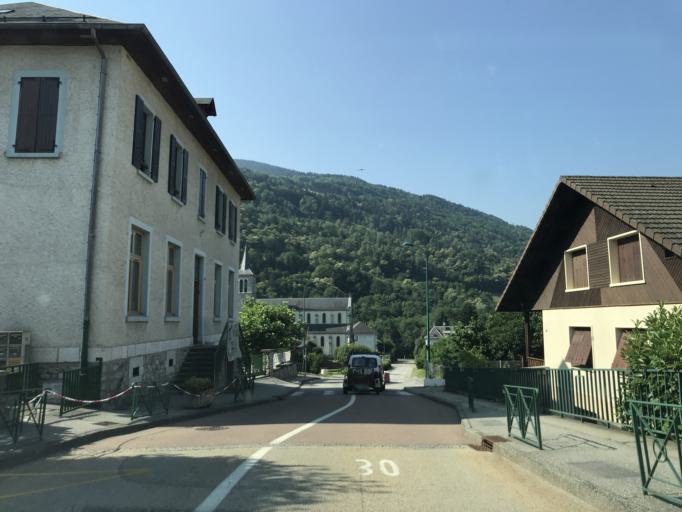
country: FR
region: Rhone-Alpes
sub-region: Departement de la Savoie
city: La Rochette
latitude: 45.4415
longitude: 6.1202
